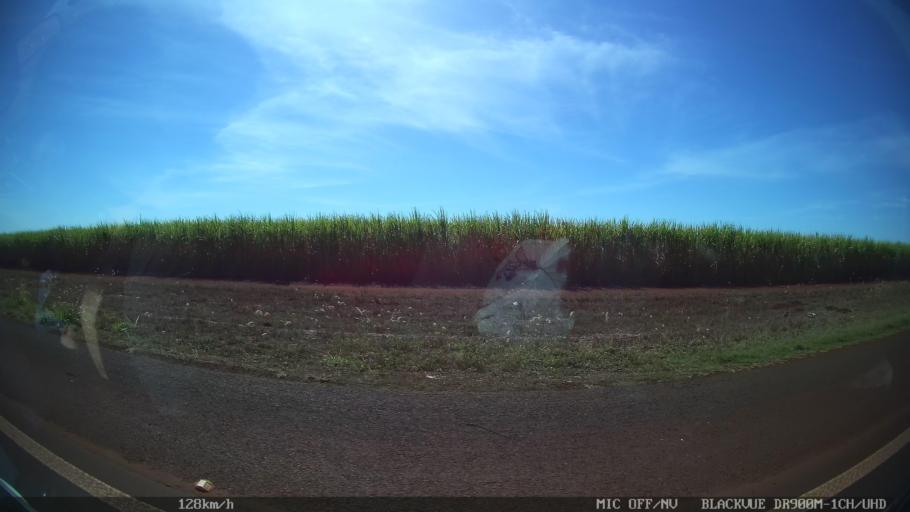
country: BR
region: Sao Paulo
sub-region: Guaira
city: Guaira
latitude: -20.4436
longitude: -48.3149
